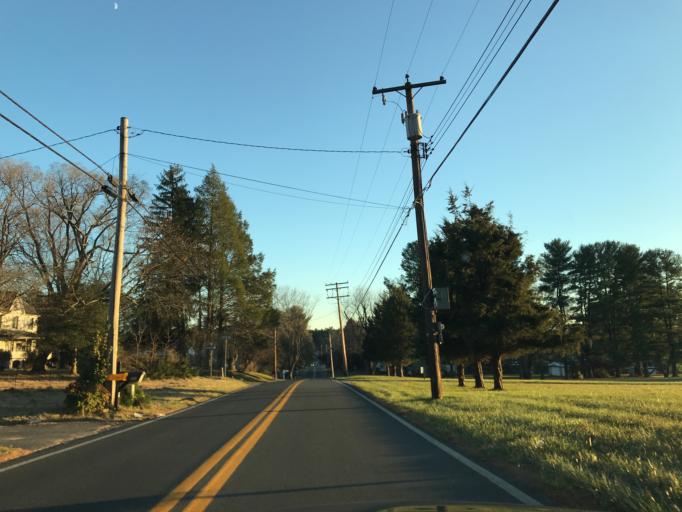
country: US
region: Maryland
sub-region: Carroll County
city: Eldersburg
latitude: 39.4006
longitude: -76.8966
